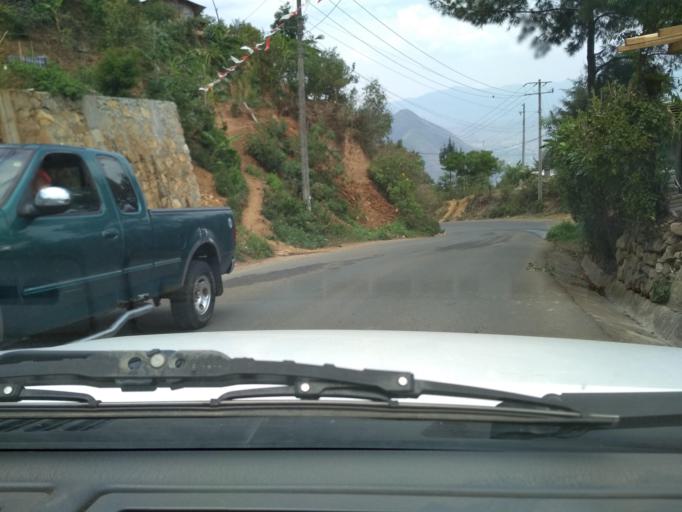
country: MX
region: Veracruz
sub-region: Camerino Z. Mendoza
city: La Cuesta
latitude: 18.7886
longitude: -97.1674
